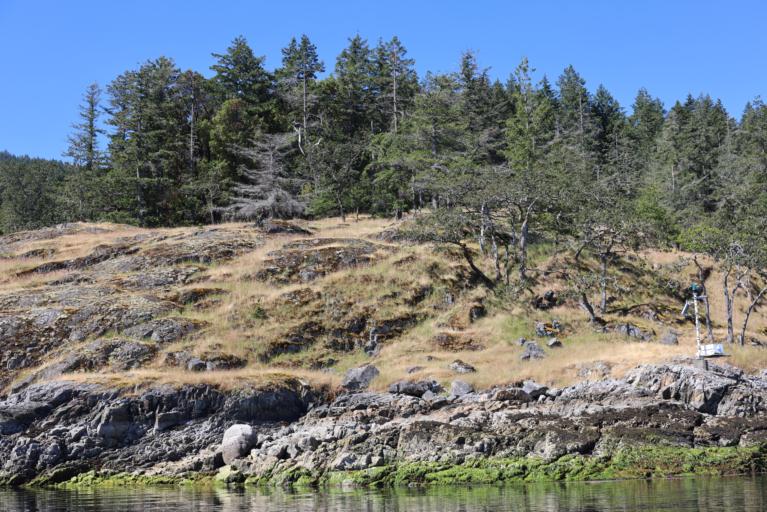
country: CA
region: British Columbia
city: North Cowichan
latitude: 48.8484
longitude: -123.5919
